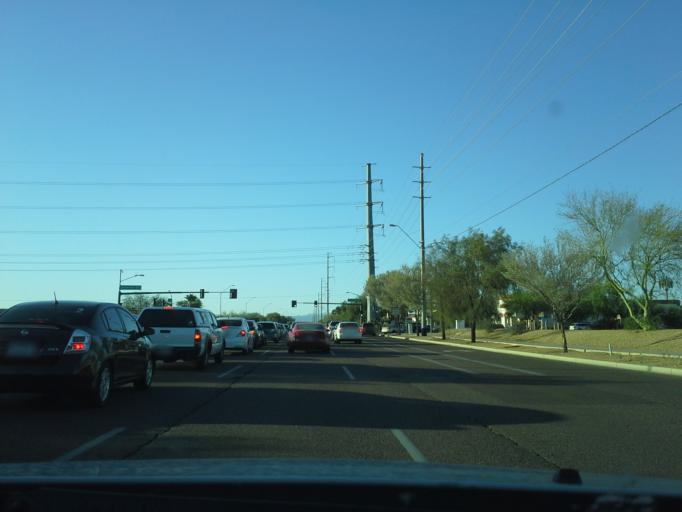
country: US
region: Arizona
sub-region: Maricopa County
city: Paradise Valley
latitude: 33.6541
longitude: -112.0135
